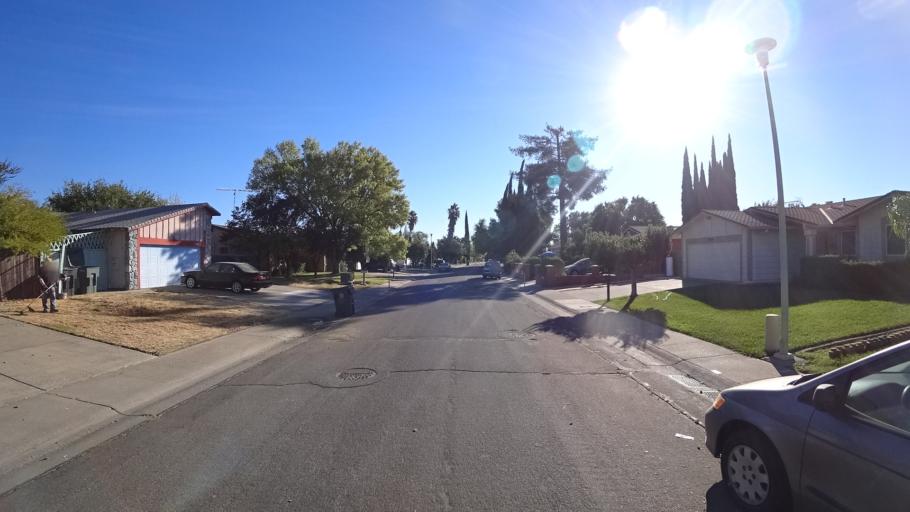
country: US
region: California
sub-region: Sacramento County
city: Parkway
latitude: 38.4853
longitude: -121.4616
